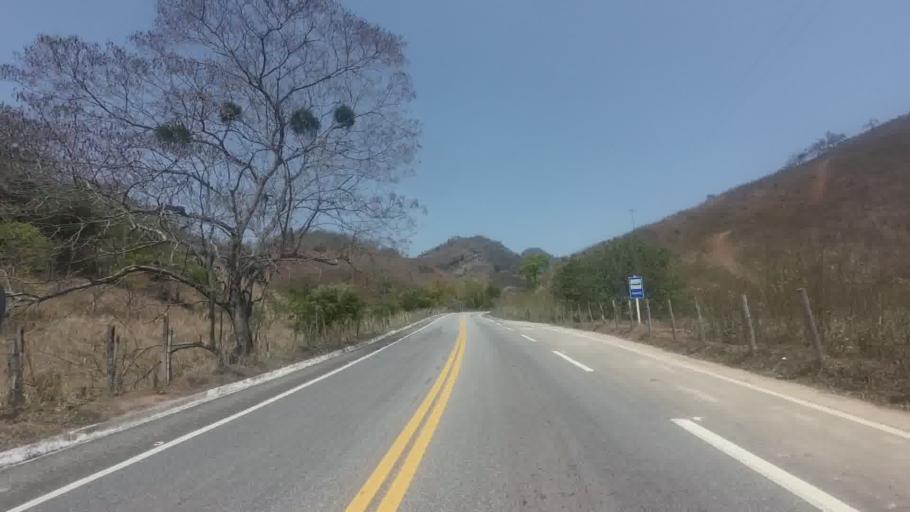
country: BR
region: Espirito Santo
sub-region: Cachoeiro De Itapemirim
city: Cachoeiro de Itapemirim
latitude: -20.8460
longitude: -41.2423
